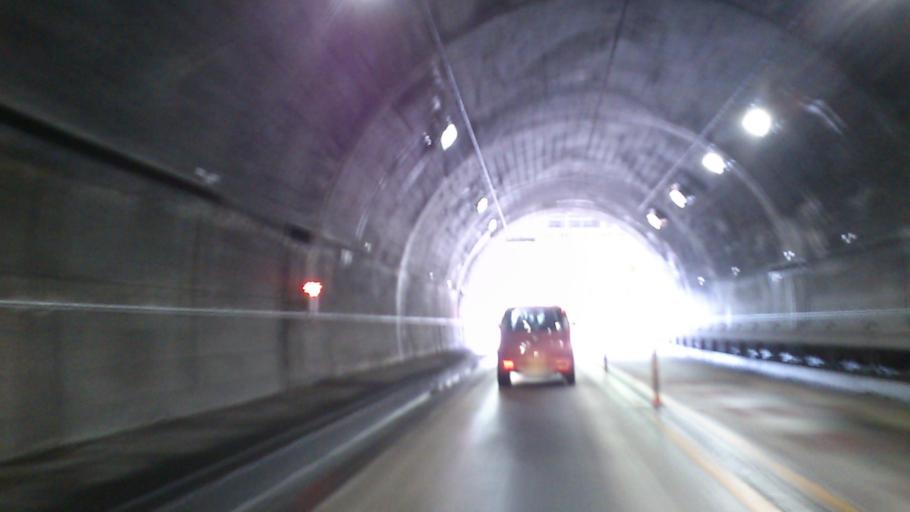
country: JP
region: Nagano
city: Saku
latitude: 36.2419
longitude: 138.6505
